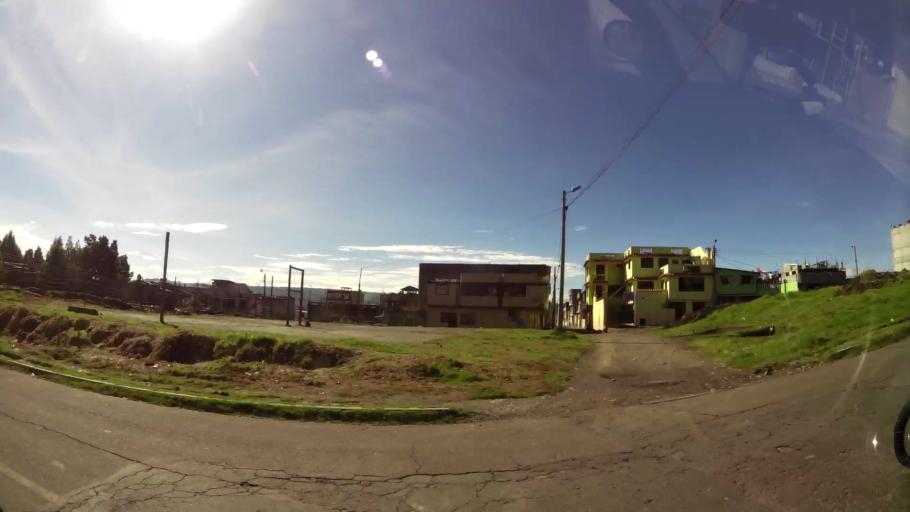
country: EC
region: Pichincha
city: Quito
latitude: -0.2923
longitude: -78.5674
